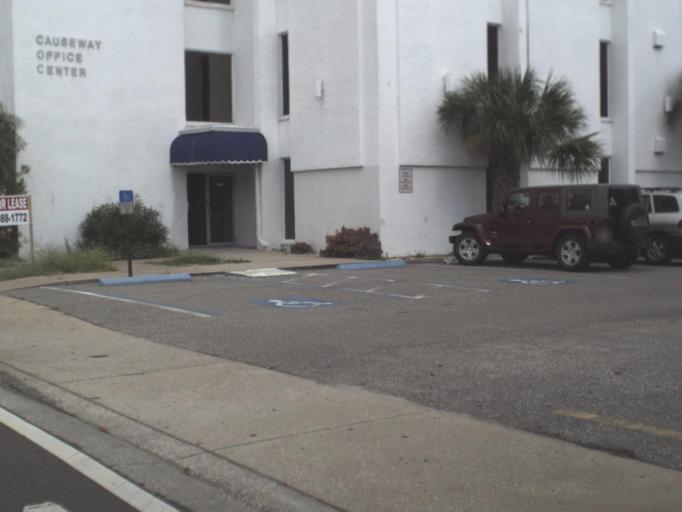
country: US
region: Florida
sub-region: Pinellas County
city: Safety Harbor
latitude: 27.9608
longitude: -82.7075
